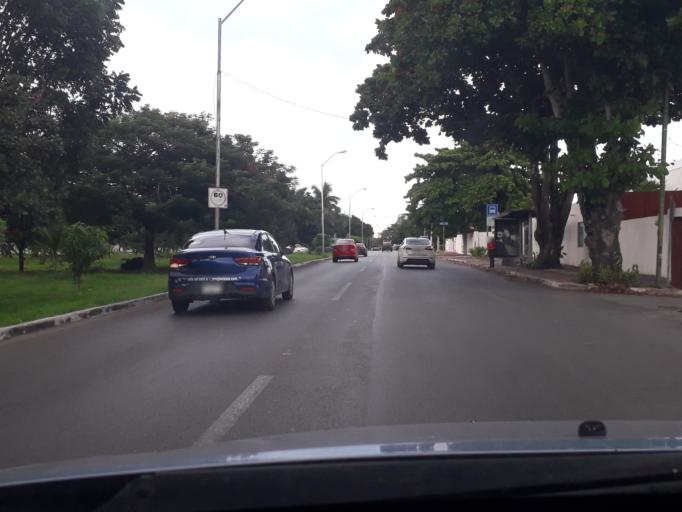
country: MX
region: Yucatan
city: Merida
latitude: 20.9850
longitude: -89.6633
